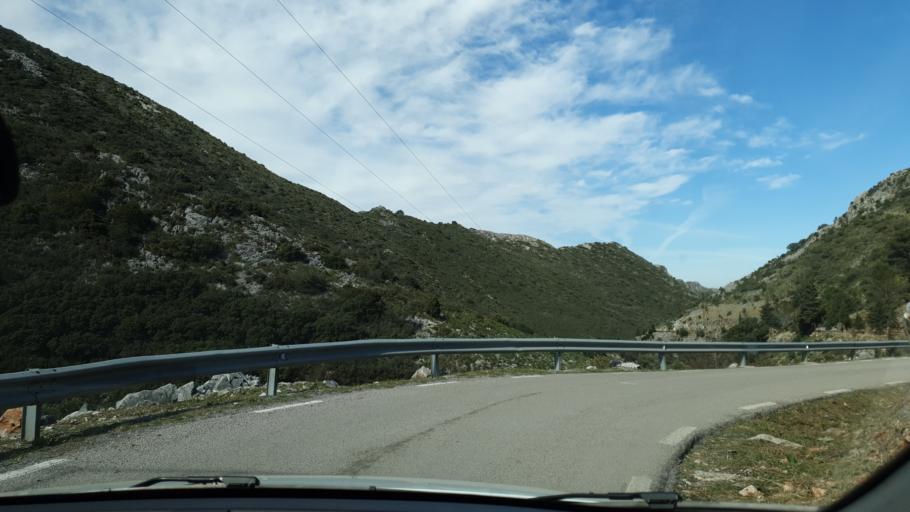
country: ES
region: Andalusia
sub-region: Provincia de Malaga
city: Ojen
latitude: 36.5829
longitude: -4.8842
